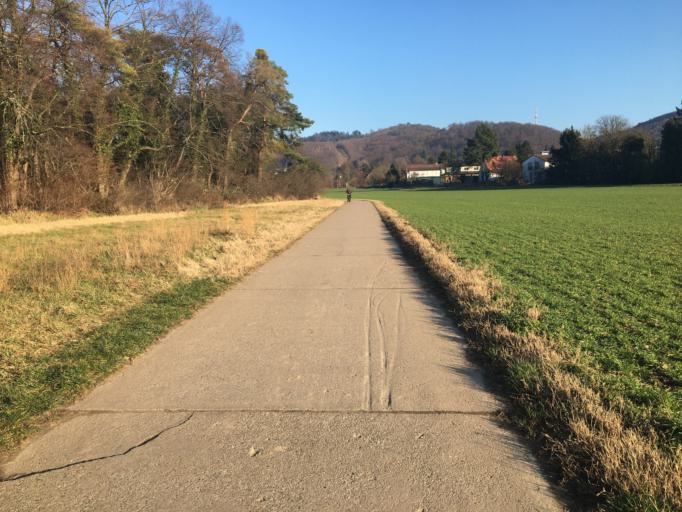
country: DE
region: Hesse
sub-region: Regierungsbezirk Darmstadt
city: Bickenbach
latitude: 49.7582
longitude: 8.6294
